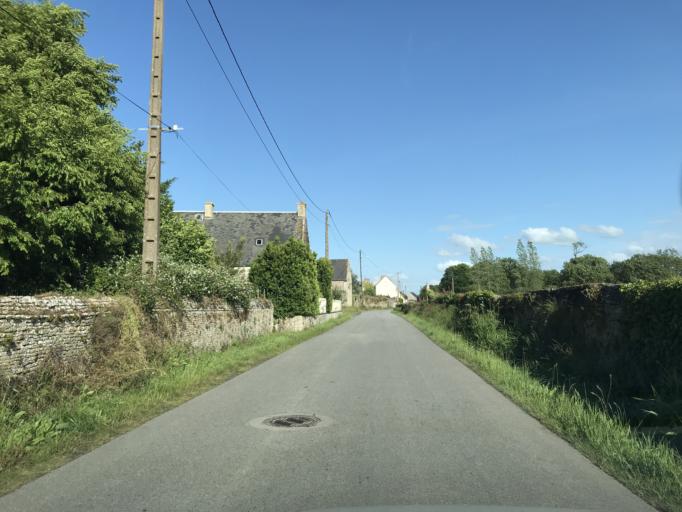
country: FR
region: Lower Normandy
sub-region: Departement du Calvados
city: Grandcamp-Maisy
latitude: 49.3802
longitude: -1.0538
